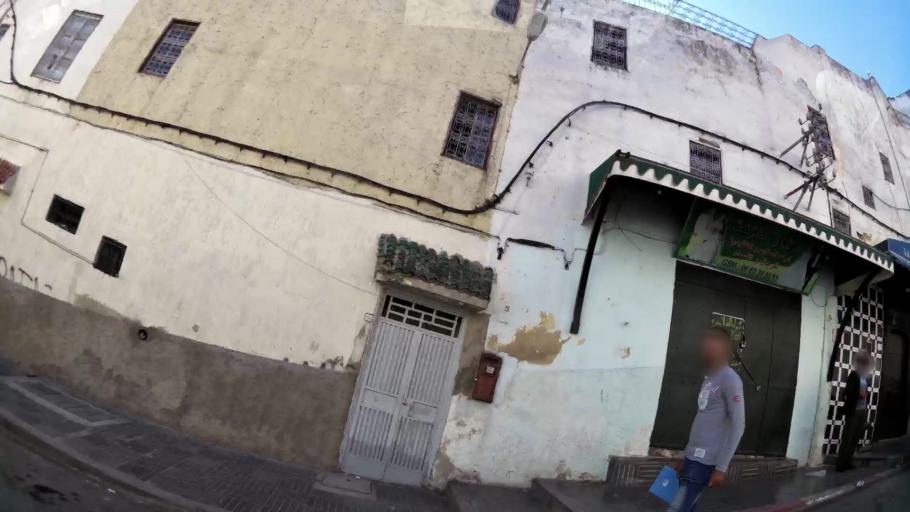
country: MA
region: Fes-Boulemane
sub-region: Fes
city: Fes
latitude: 34.0640
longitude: -4.9640
